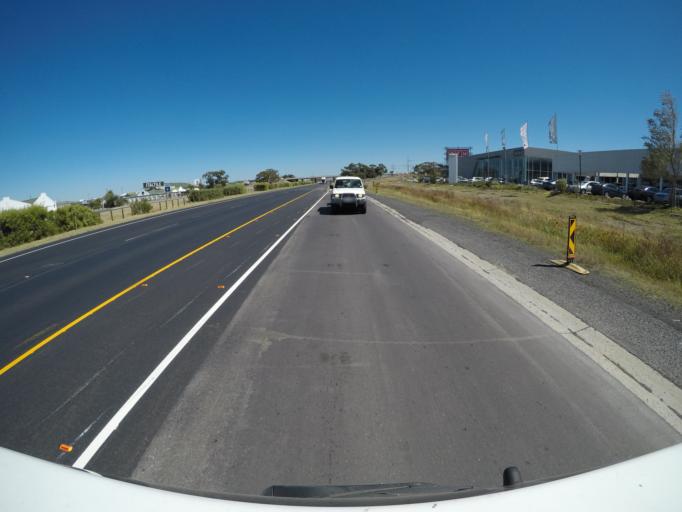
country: ZA
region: Western Cape
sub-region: Cape Winelands District Municipality
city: Stellenbosch
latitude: -34.0792
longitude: 18.8237
